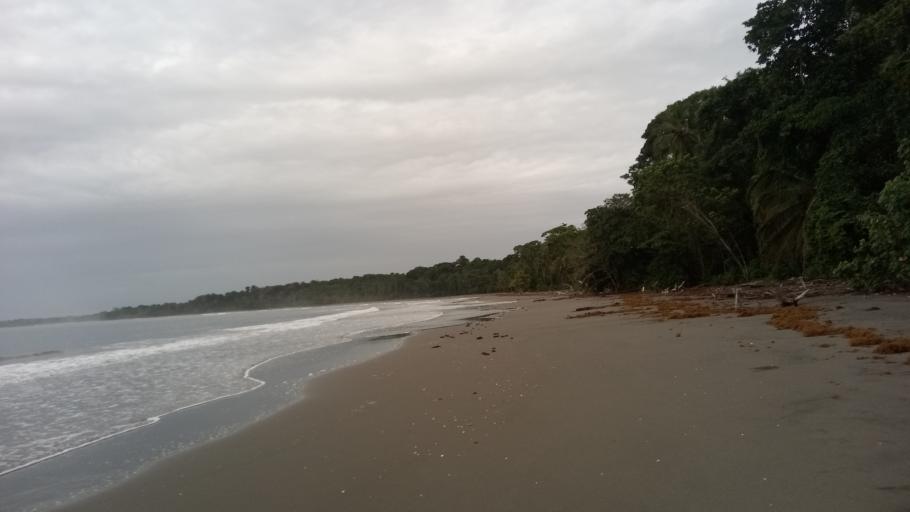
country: CR
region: Limon
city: Sixaola
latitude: 9.6219
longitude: -82.6206
